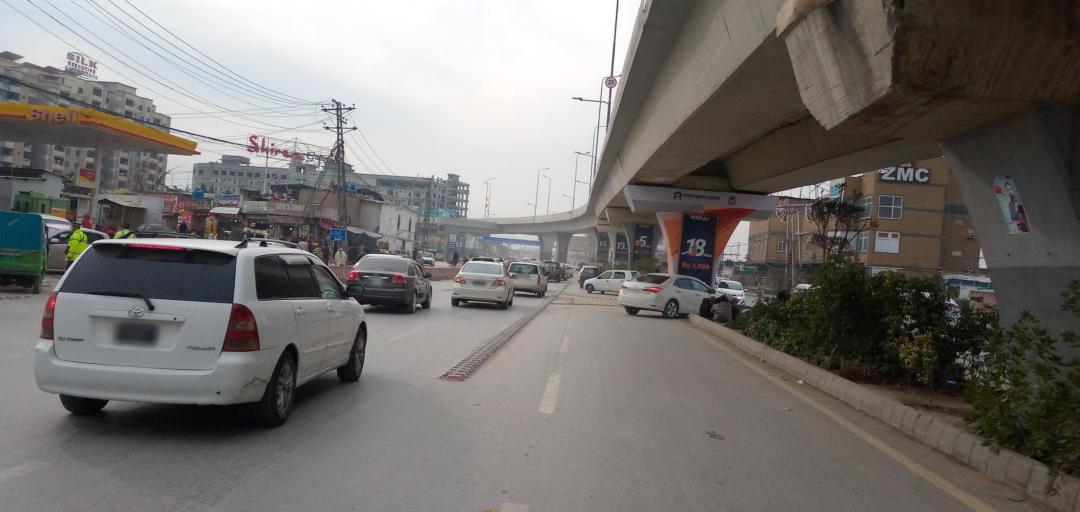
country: PK
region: Khyber Pakhtunkhwa
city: Peshawar
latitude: 33.9974
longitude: 71.4666
